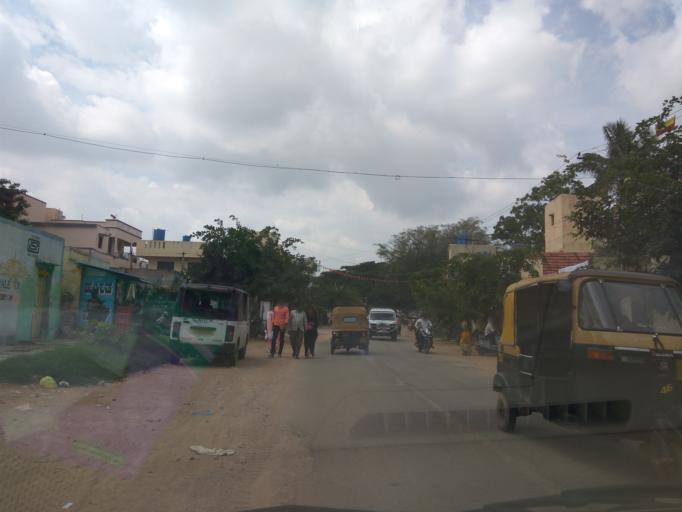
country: IN
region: Karnataka
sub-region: Kolar
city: Kolar
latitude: 13.1329
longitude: 78.1354
